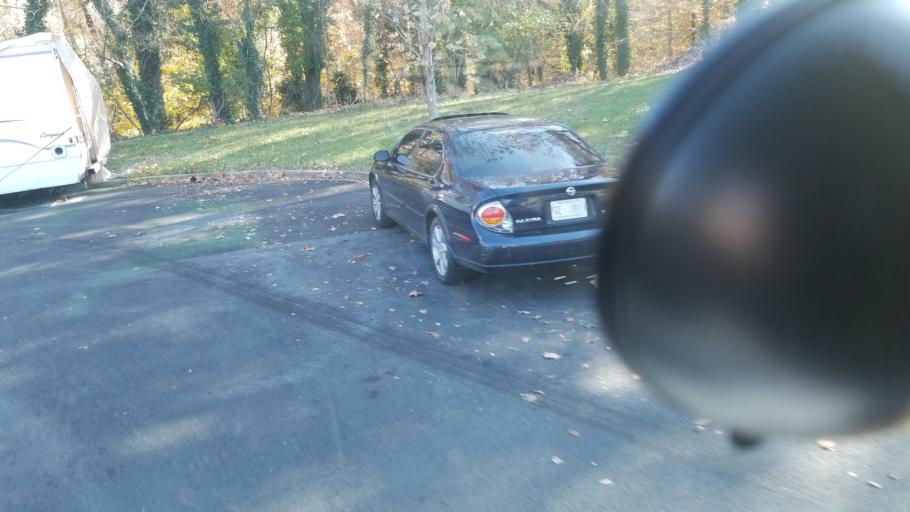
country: US
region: Maryland
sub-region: Prince George's County
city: Coral Hills
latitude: 38.8828
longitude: -76.9454
